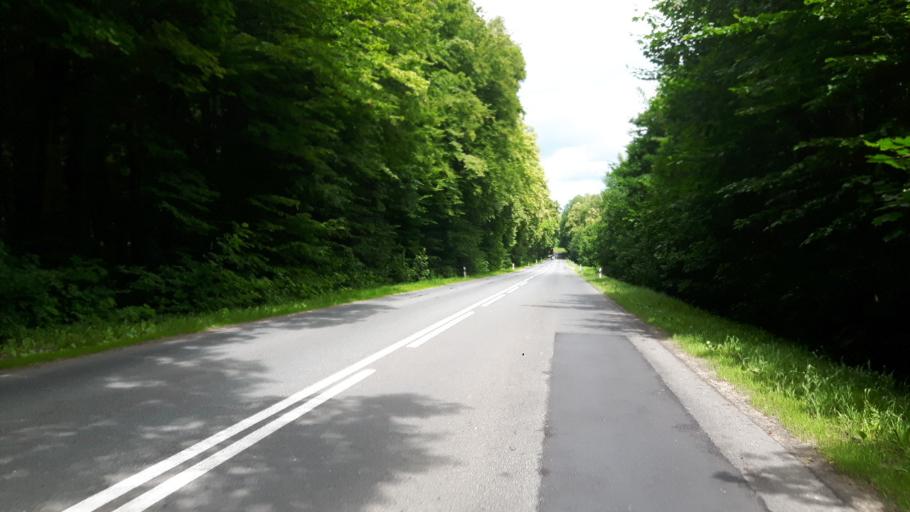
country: RU
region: Kaliningrad
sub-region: Zelenogradskiy Rayon
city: Zelenogradsk
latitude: 54.8310
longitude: 20.4315
